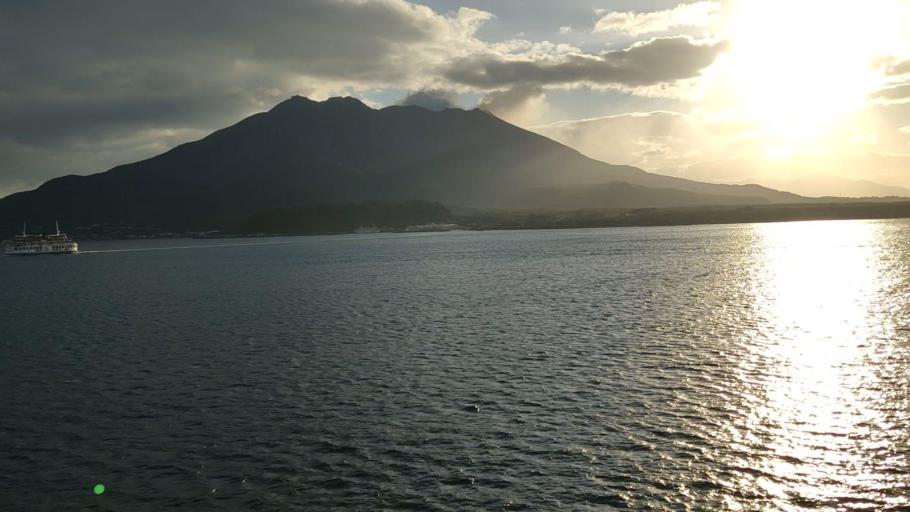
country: JP
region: Kagoshima
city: Kagoshima-shi
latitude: 31.5962
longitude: 130.5788
